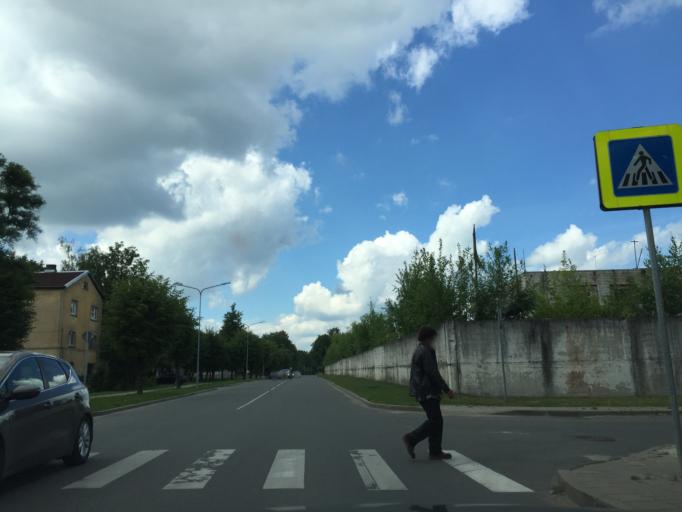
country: LV
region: Jelgava
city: Jelgava
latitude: 56.6549
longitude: 23.7531
